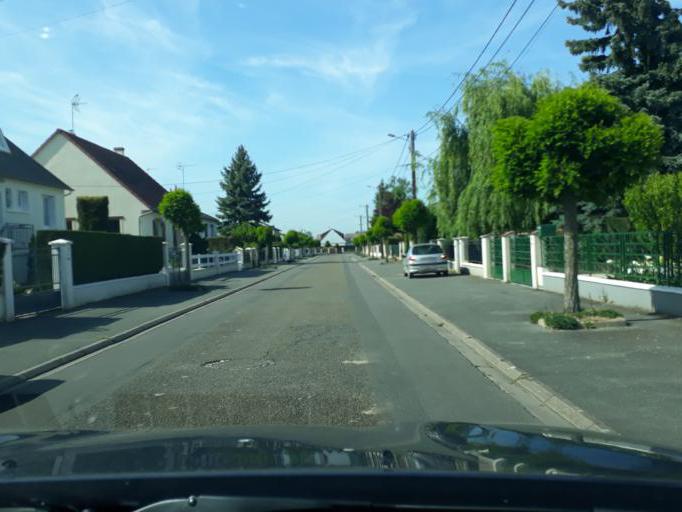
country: FR
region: Centre
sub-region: Departement du Loiret
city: Chevilly
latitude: 48.0259
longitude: 1.8692
